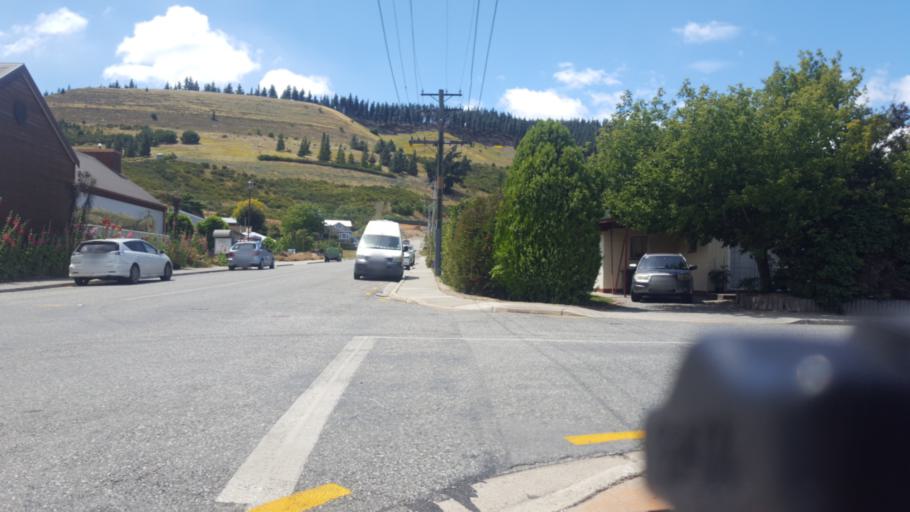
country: NZ
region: Otago
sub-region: Queenstown-Lakes District
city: Wanaka
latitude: -45.1866
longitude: 169.3173
